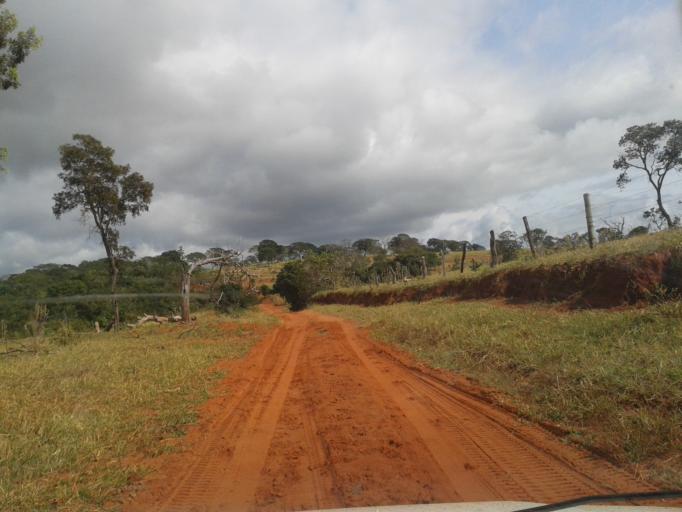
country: BR
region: Minas Gerais
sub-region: Campina Verde
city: Campina Verde
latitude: -19.4143
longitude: -49.6607
